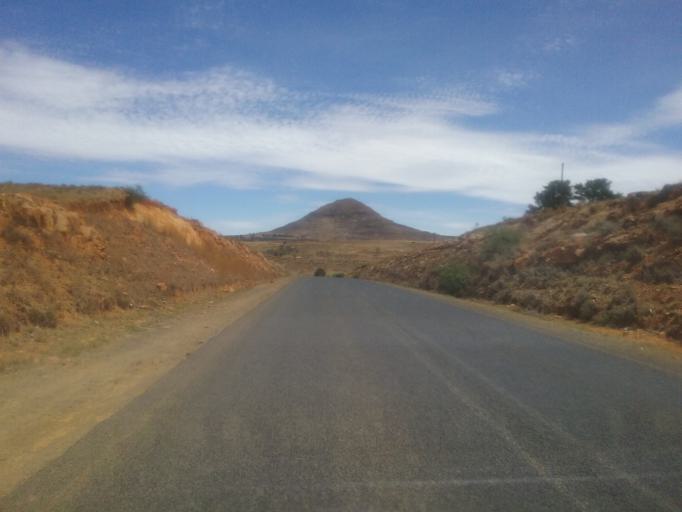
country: LS
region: Mafeteng
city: Mafeteng
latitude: -29.9662
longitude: 27.3035
